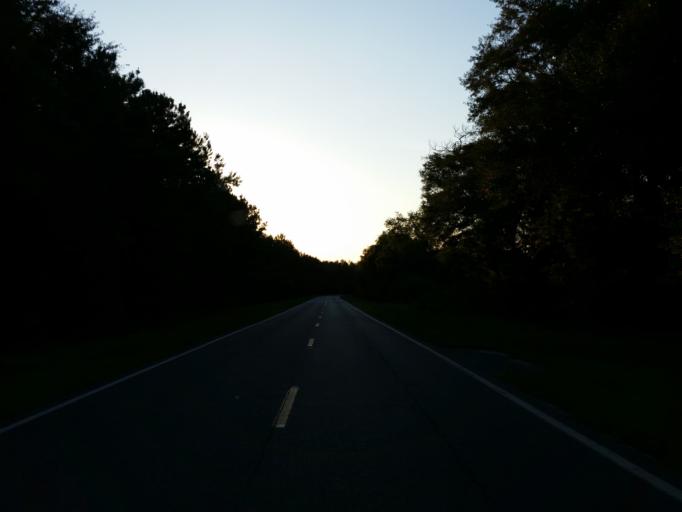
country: US
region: Georgia
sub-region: Berrien County
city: Nashville
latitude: 31.1983
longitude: -83.2243
